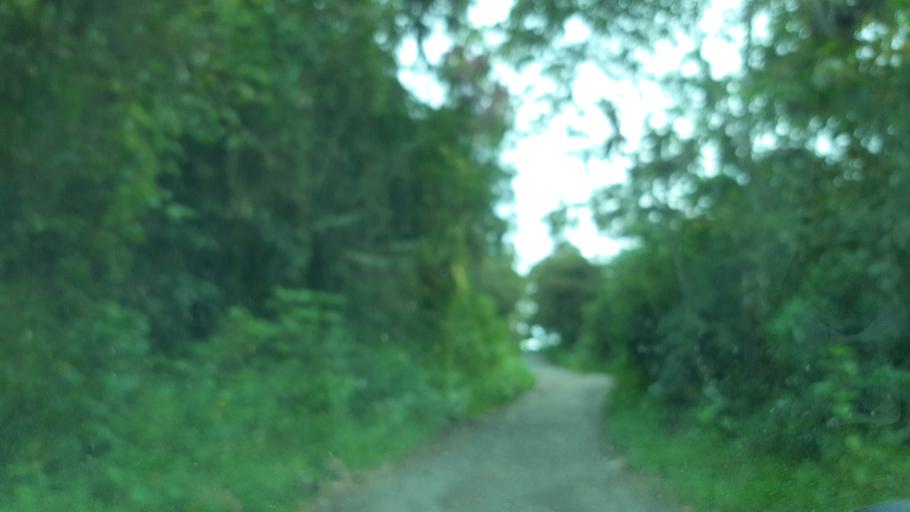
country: CO
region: Boyaca
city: Garagoa
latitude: 4.9970
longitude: -73.3291
